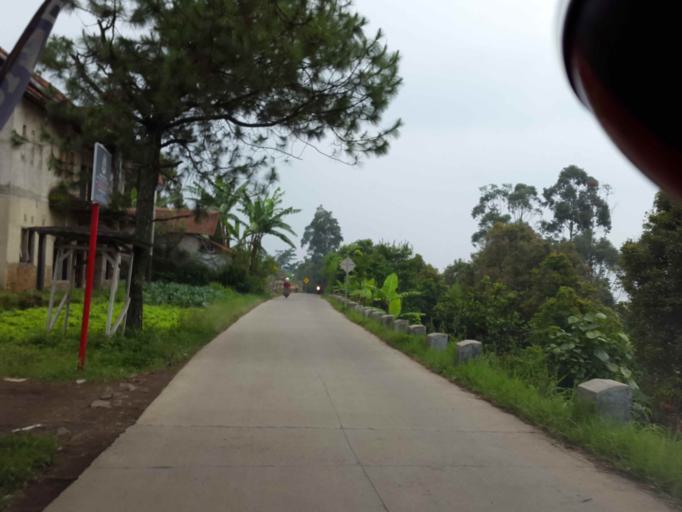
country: ID
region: West Java
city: Lembang
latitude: -6.8210
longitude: 107.5865
